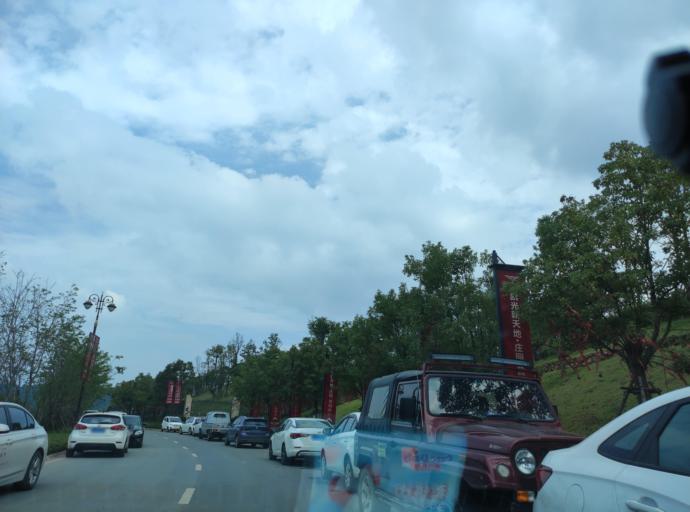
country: CN
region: Jiangxi Sheng
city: Pingxiang
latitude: 27.6636
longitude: 113.9119
